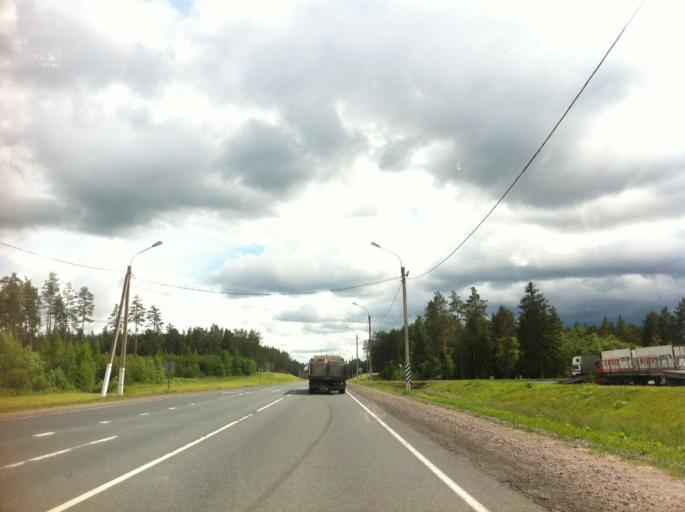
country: RU
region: Leningrad
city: Luga
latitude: 58.7145
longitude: 29.8788
